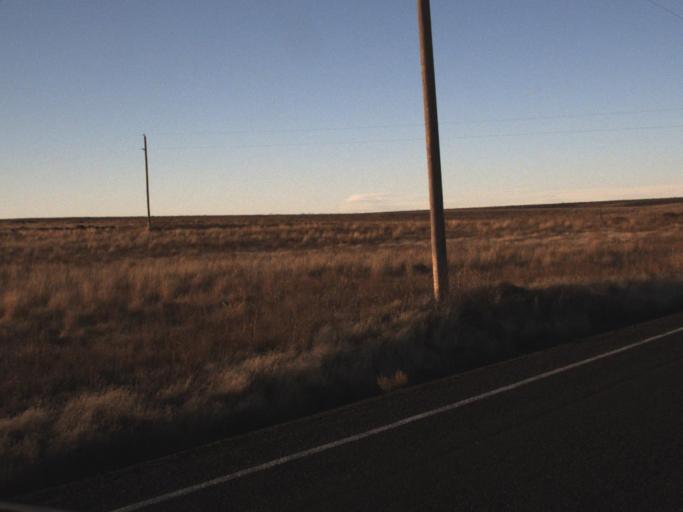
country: US
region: Washington
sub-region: Franklin County
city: Connell
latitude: 46.7215
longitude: -118.5481
